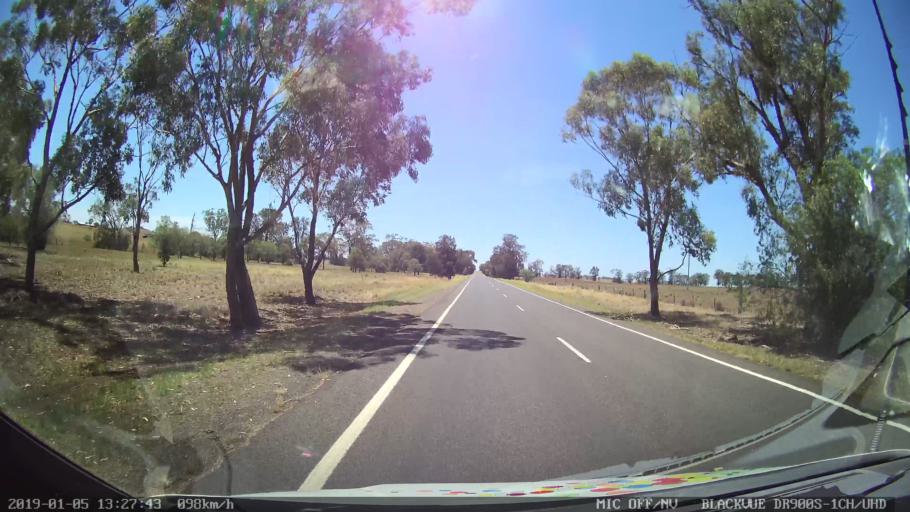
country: AU
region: New South Wales
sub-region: Gunnedah
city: Gunnedah
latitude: -31.0422
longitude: 150.0331
